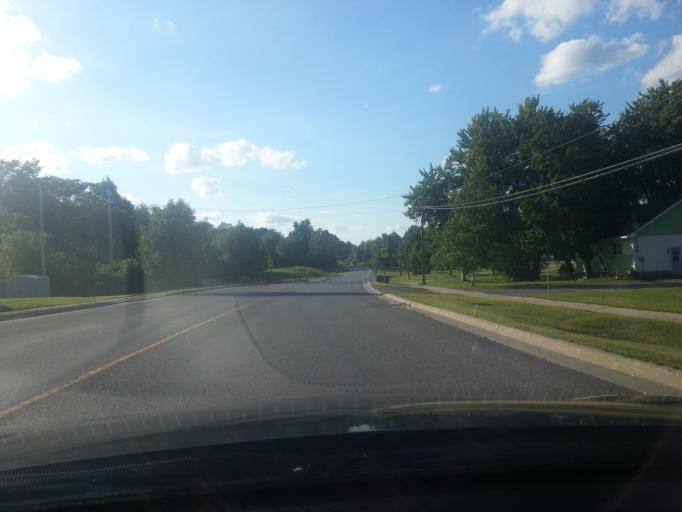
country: CA
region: Ontario
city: Perth
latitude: 45.0226
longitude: -76.3705
